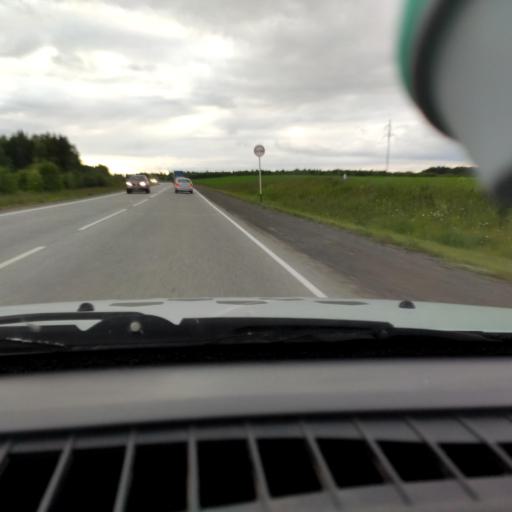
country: RU
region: Perm
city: Lyamino
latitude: 58.3283
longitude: 57.6776
